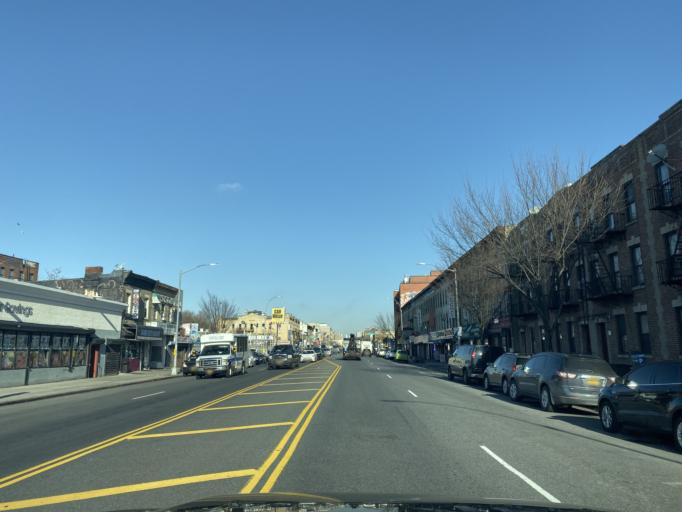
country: US
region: New York
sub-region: Kings County
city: Brooklyn
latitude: 40.6402
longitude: -73.9690
